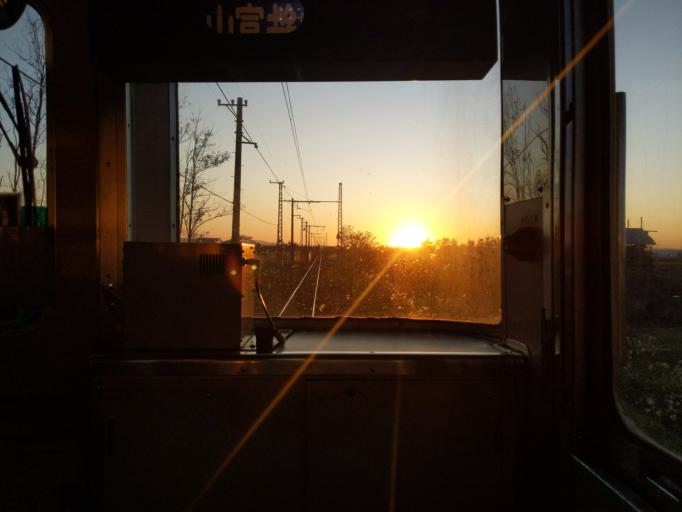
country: JP
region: Toyama
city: Toyama-shi
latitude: 36.7031
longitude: 137.2828
